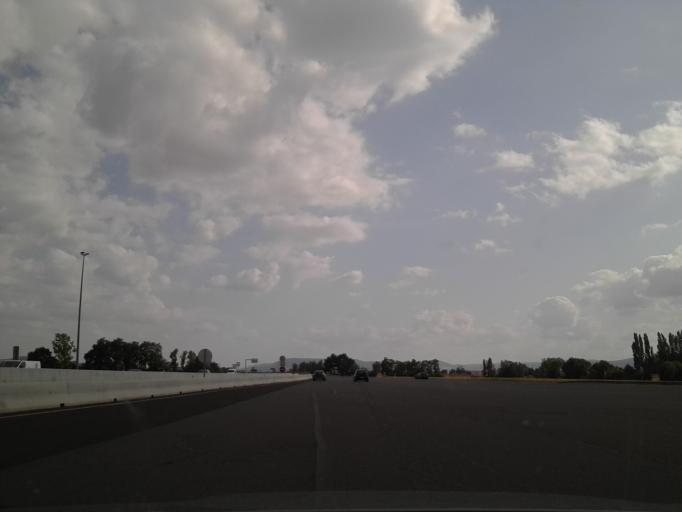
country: FR
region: Auvergne
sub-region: Departement du Puy-de-Dome
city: Gerzat
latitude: 45.8408
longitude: 3.1609
